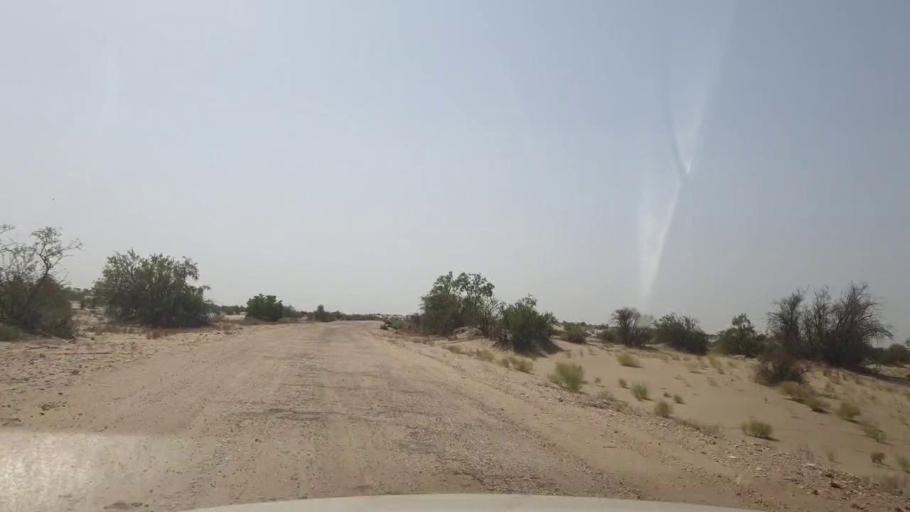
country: PK
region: Sindh
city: Rohri
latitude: 27.4411
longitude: 69.2414
